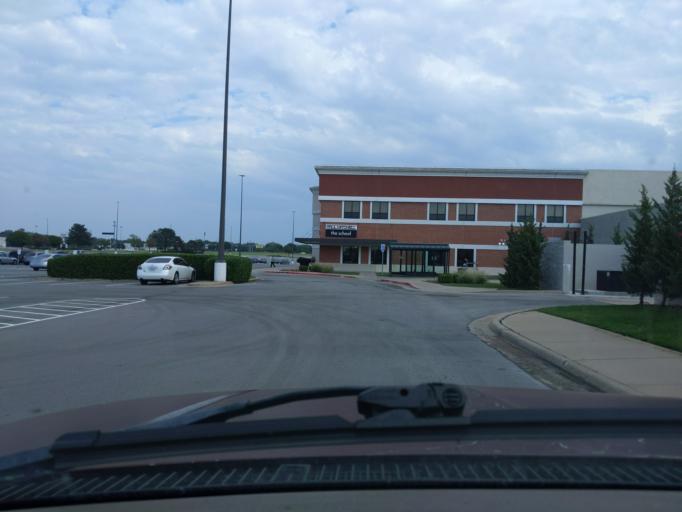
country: US
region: Oklahoma
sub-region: Tulsa County
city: Broken Arrow
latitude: 36.1323
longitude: -95.8210
